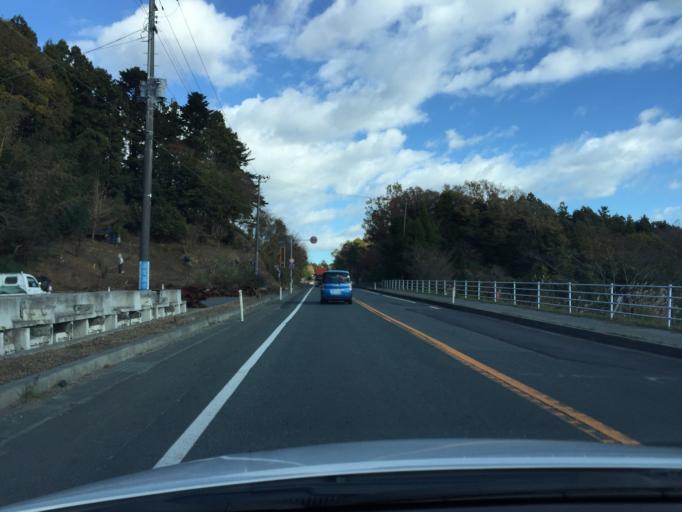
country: JP
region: Fukushima
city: Namie
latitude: 37.3265
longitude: 141.0154
